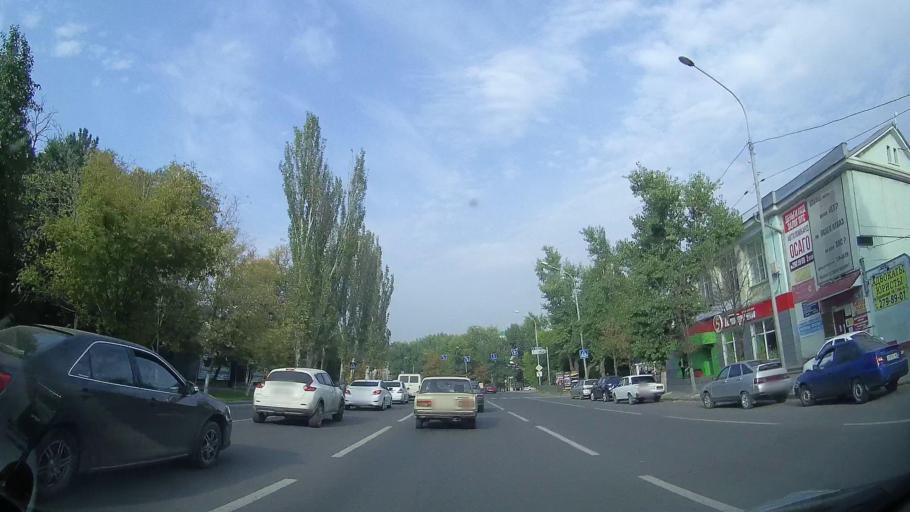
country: RU
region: Rostov
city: Rostov-na-Donu
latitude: 47.2397
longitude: 39.7012
